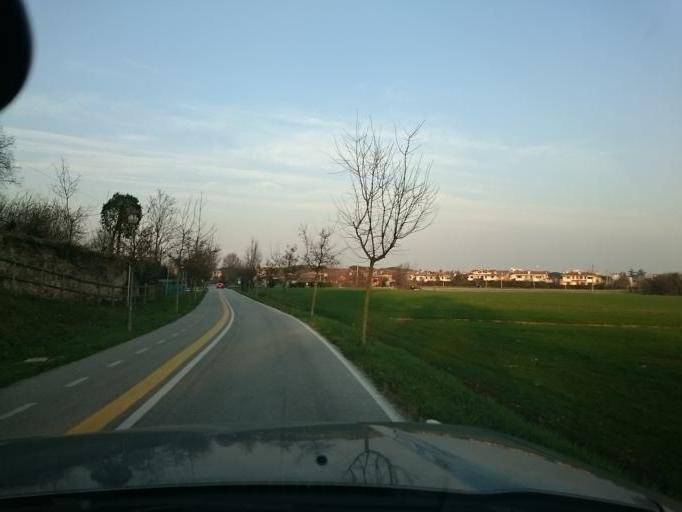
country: IT
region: Veneto
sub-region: Provincia di Padova
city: Montegrotto Terme
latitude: 45.3438
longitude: 11.7684
